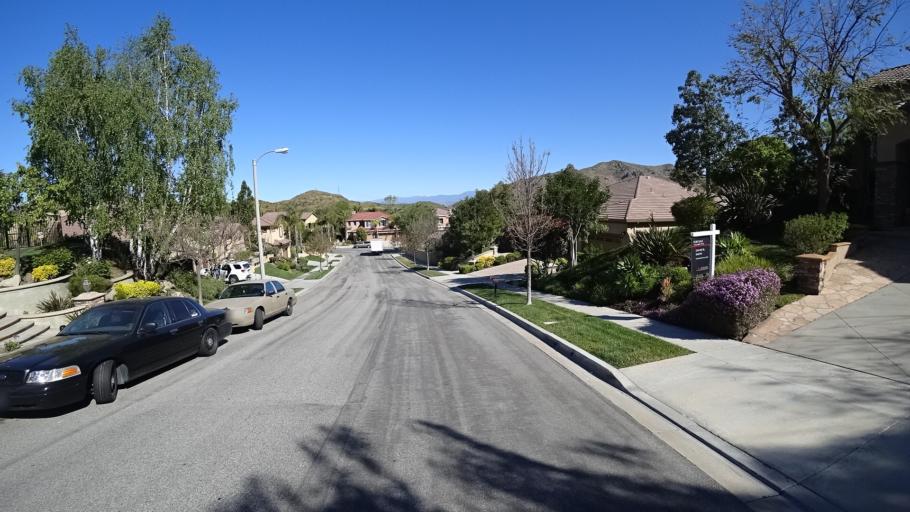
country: US
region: California
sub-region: Ventura County
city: Casa Conejo
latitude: 34.1671
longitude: -118.9869
